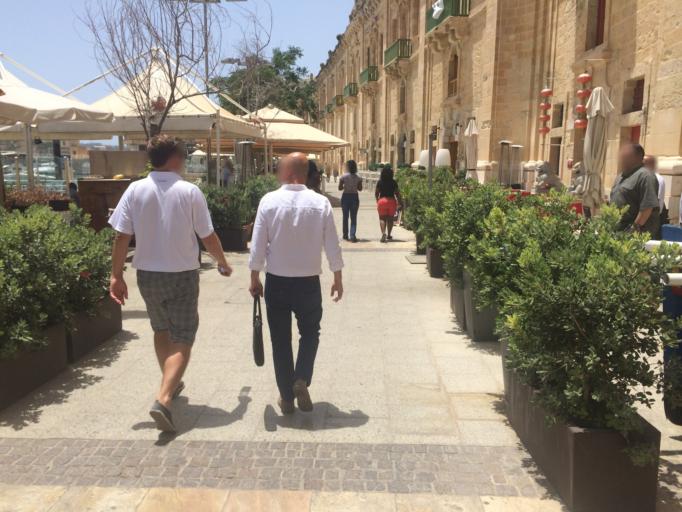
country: MT
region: Il-Furjana
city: Floriana
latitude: 35.8898
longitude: 14.5093
